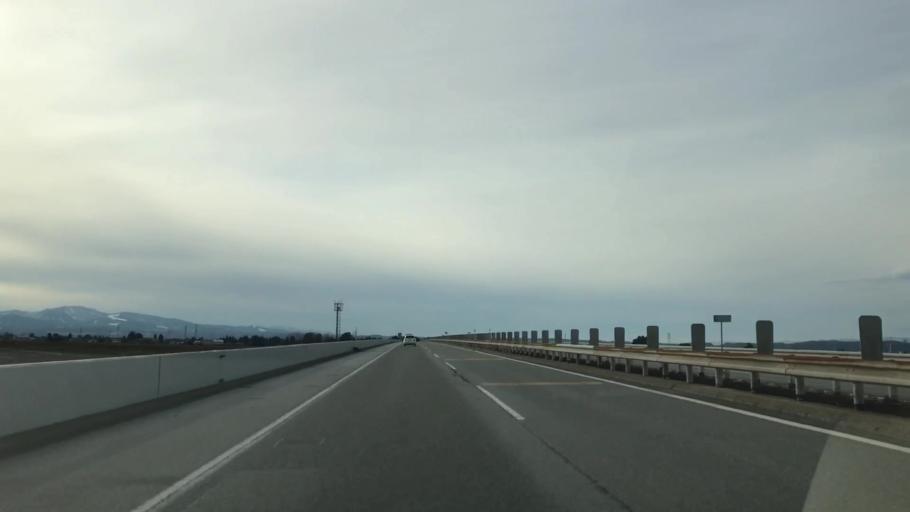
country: JP
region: Toyama
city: Toyama-shi
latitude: 36.6677
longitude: 137.2850
